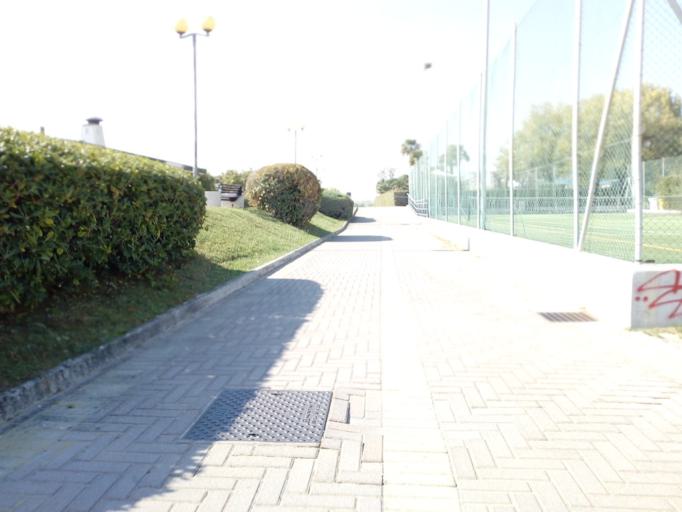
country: IT
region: Veneto
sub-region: Provincia di Venezia
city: Bibione
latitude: 45.6328
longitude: 13.0502
